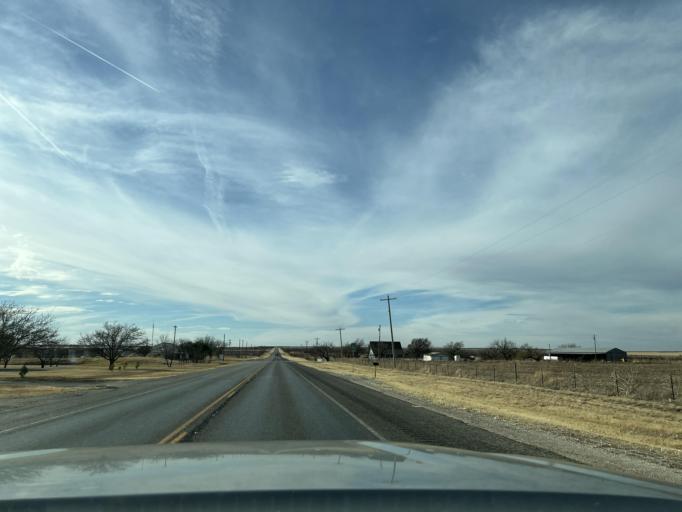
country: US
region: Texas
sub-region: Jones County
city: Anson
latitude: 32.7519
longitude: -99.9207
